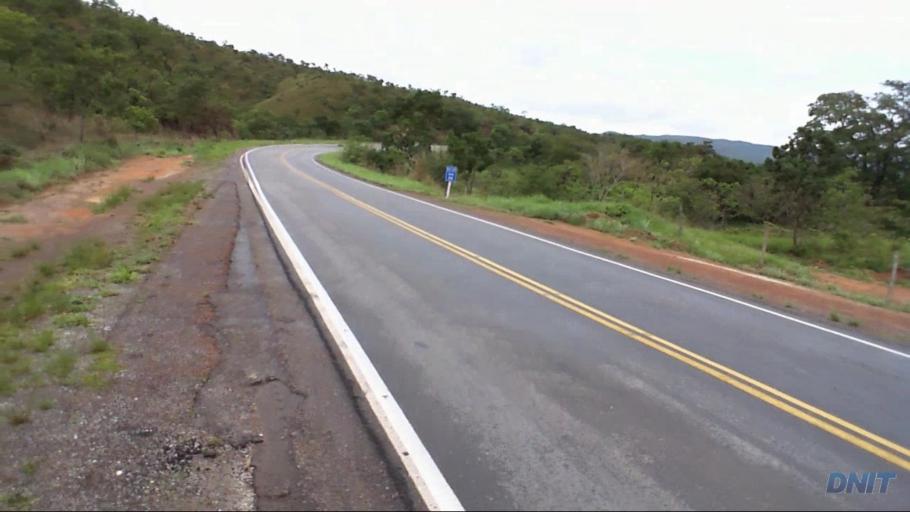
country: BR
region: Goias
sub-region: Padre Bernardo
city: Padre Bernardo
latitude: -15.4939
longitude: -48.2247
